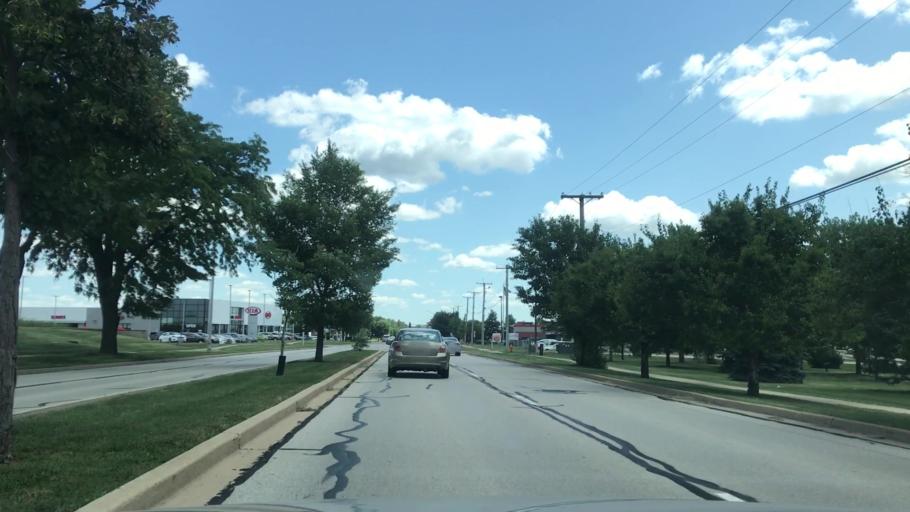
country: US
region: Illinois
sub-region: DuPage County
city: Naperville
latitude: 41.7641
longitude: -88.1899
